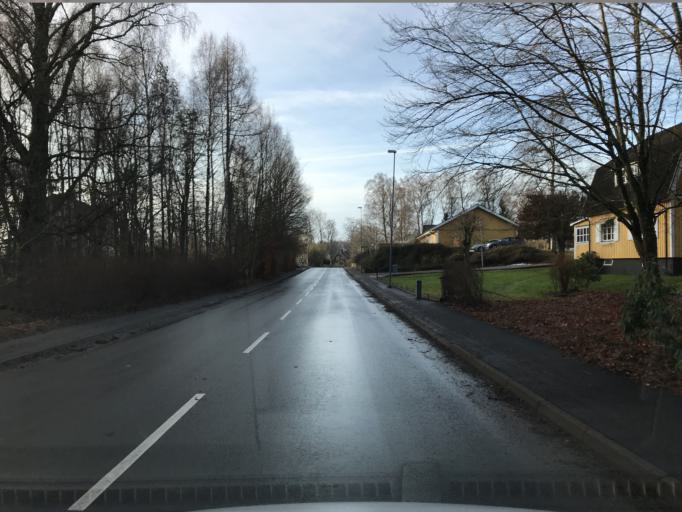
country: SE
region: Skane
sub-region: Hassleholms Kommun
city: Bjarnum
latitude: 56.2988
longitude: 13.7269
